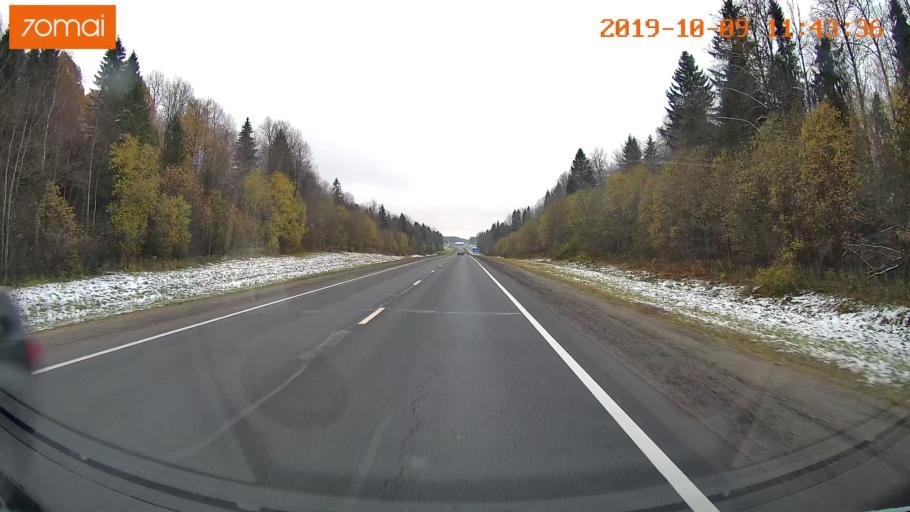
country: RU
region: Vologda
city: Gryazovets
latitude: 58.8945
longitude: 40.1865
